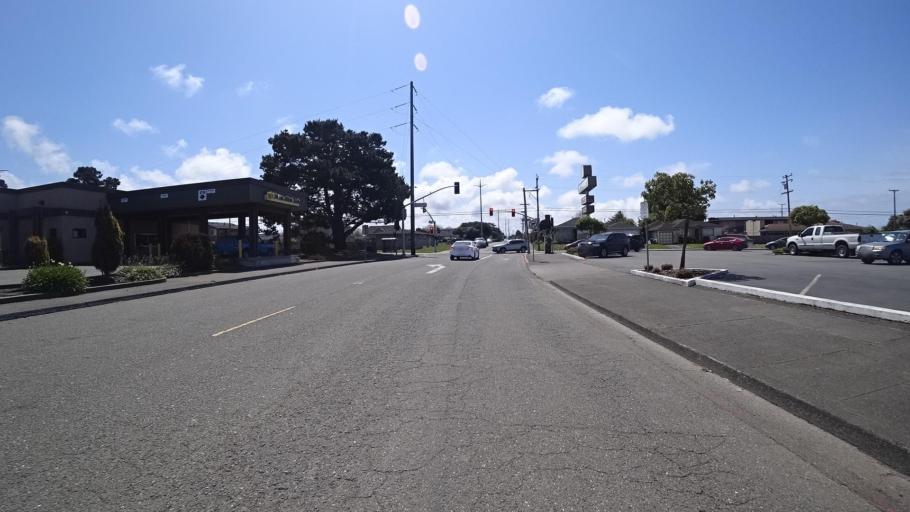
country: US
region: California
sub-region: Humboldt County
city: Bayview
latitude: 40.7810
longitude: -124.1804
